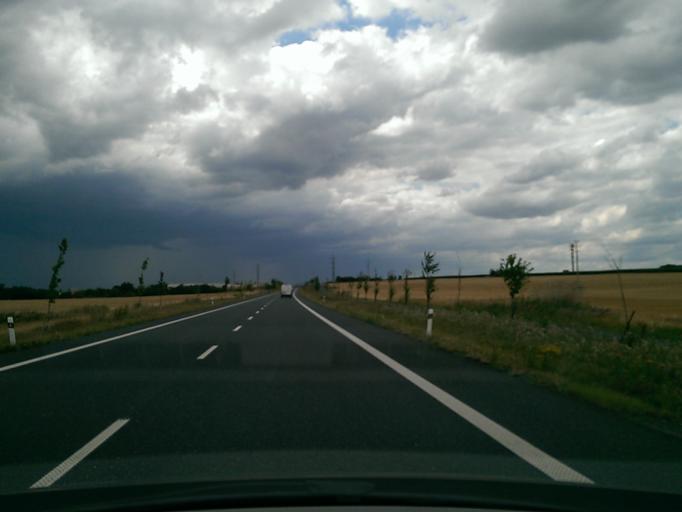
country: CZ
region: Central Bohemia
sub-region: Okres Nymburk
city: Nymburk
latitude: 50.1971
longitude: 15.0602
